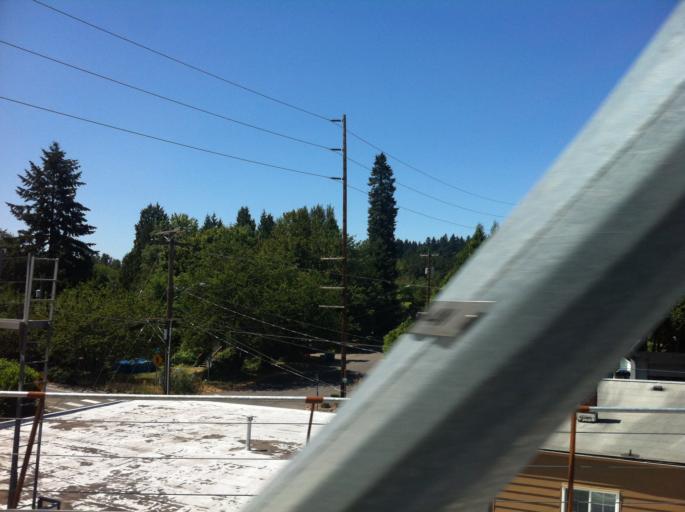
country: US
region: Oregon
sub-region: Clackamas County
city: Milwaukie
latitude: 45.4375
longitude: -122.6403
